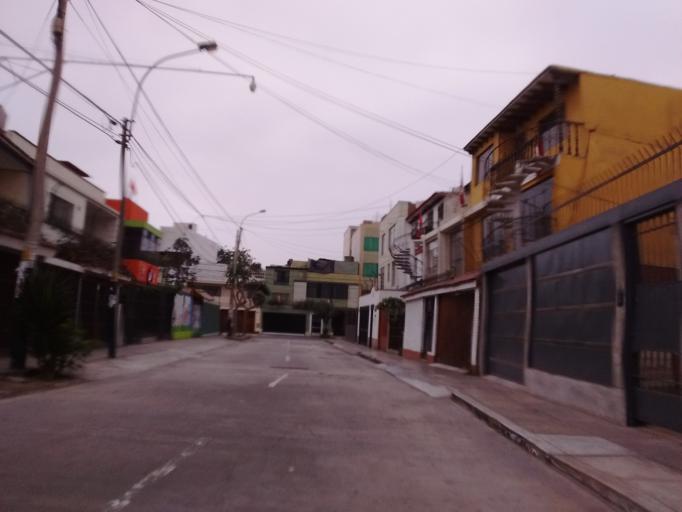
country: PE
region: Lima
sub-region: Lima
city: San Isidro
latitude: -12.0765
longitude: -77.0672
